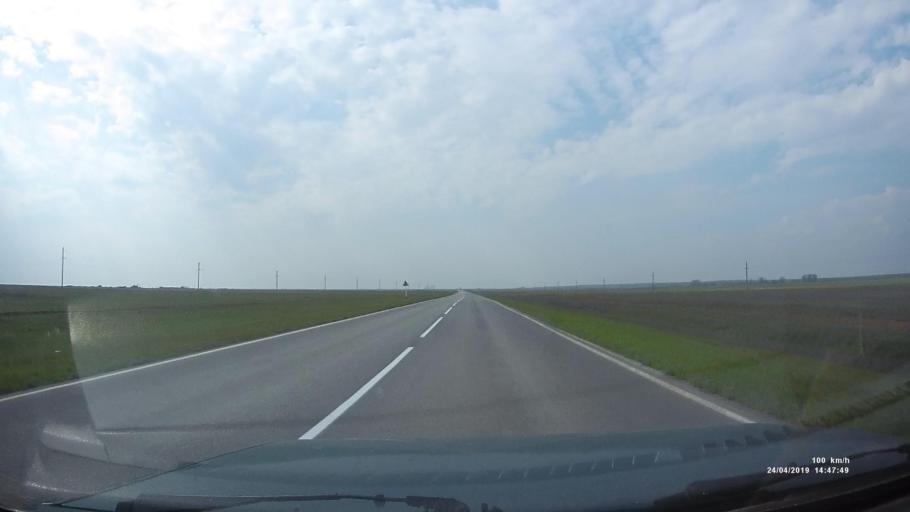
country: RU
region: Rostov
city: Remontnoye
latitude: 46.4951
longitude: 43.7666
